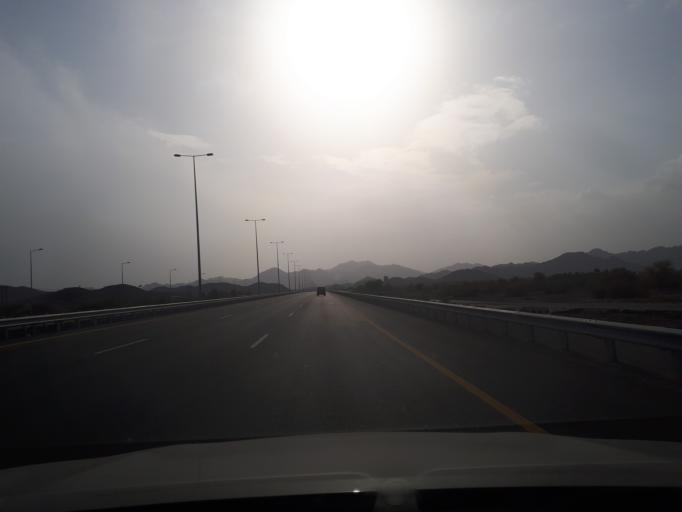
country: OM
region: Ash Sharqiyah
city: Ibra'
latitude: 22.8405
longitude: 58.3826
